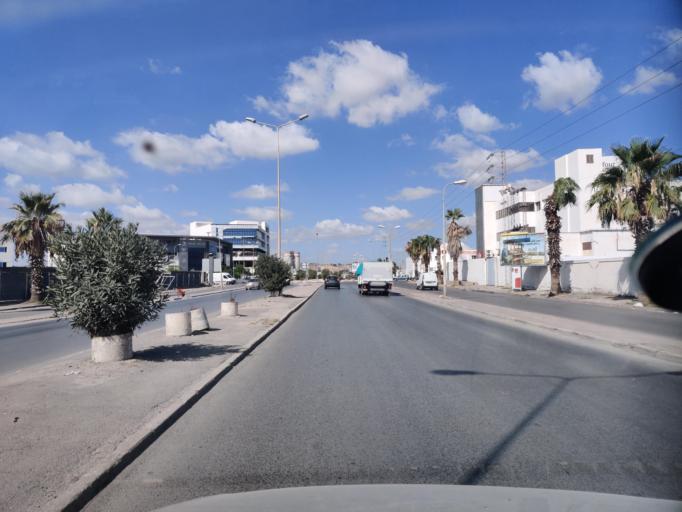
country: TN
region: Bin 'Arus
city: Ben Arous
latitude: 36.7751
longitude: 10.2161
